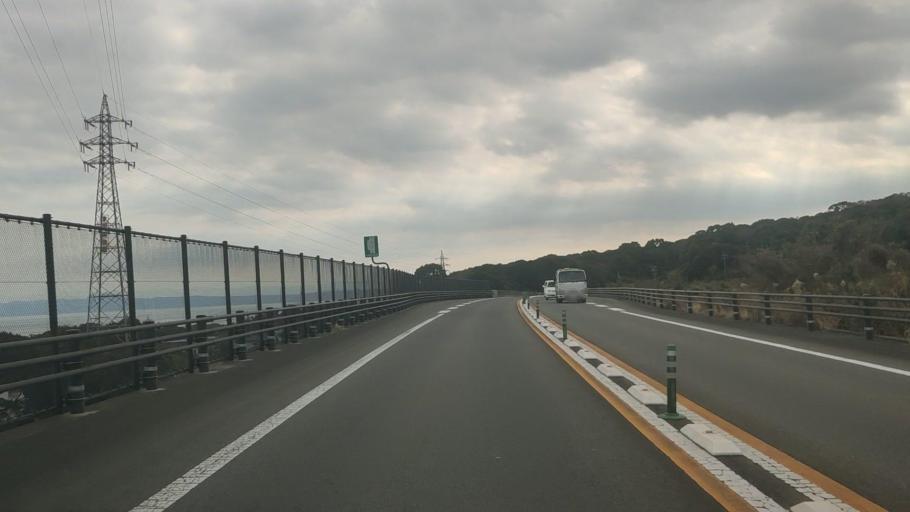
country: JP
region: Nagasaki
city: Shimabara
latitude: 32.7821
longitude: 130.3542
